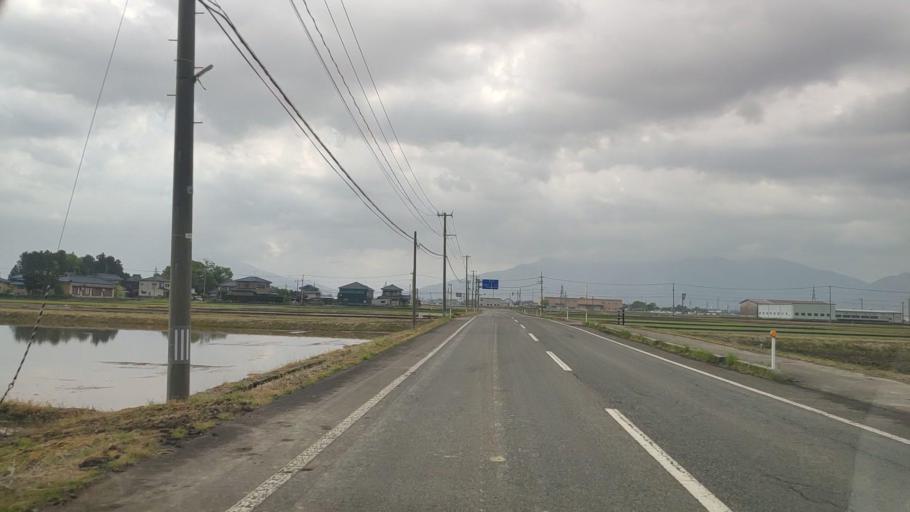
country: JP
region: Niigata
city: Gosen
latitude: 37.7292
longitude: 139.1589
